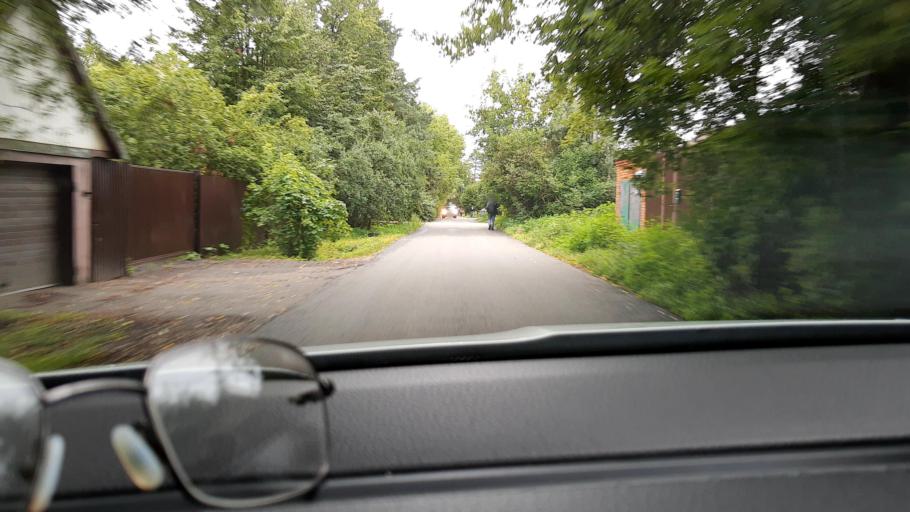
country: RU
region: Moskovskaya
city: Kokoshkino
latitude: 55.5944
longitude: 37.1728
